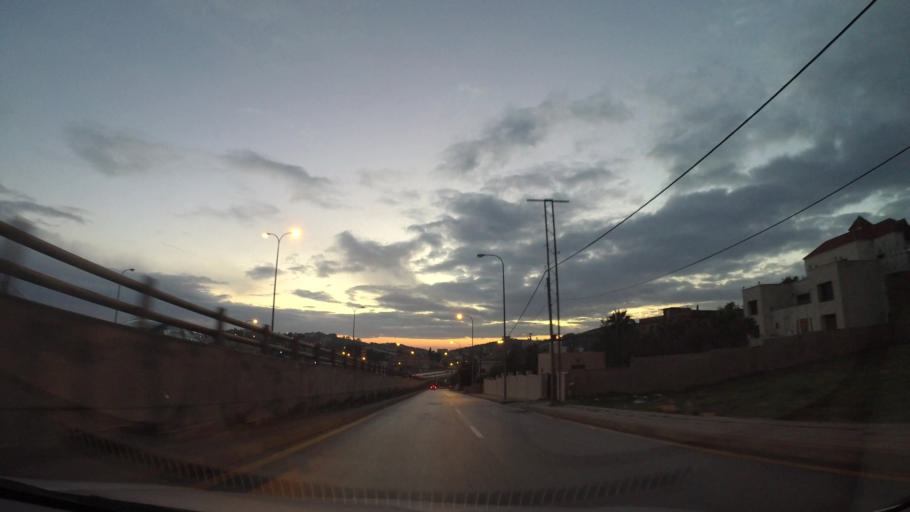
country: JO
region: Amman
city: Al Jubayhah
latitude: 32.0281
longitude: 35.8020
